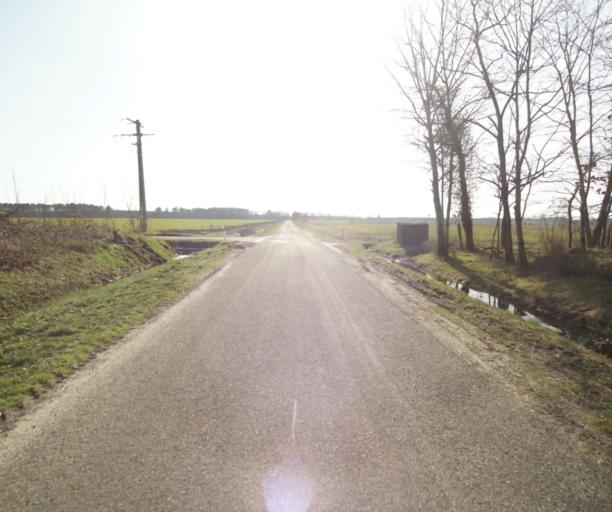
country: FR
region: Aquitaine
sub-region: Departement des Landes
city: Roquefort
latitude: 44.1545
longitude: -0.1703
